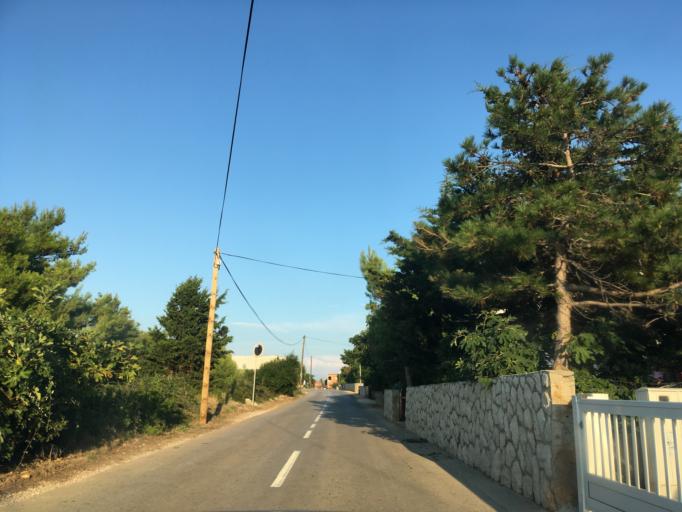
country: HR
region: Zadarska
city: Vir
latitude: 44.3056
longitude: 15.0926
